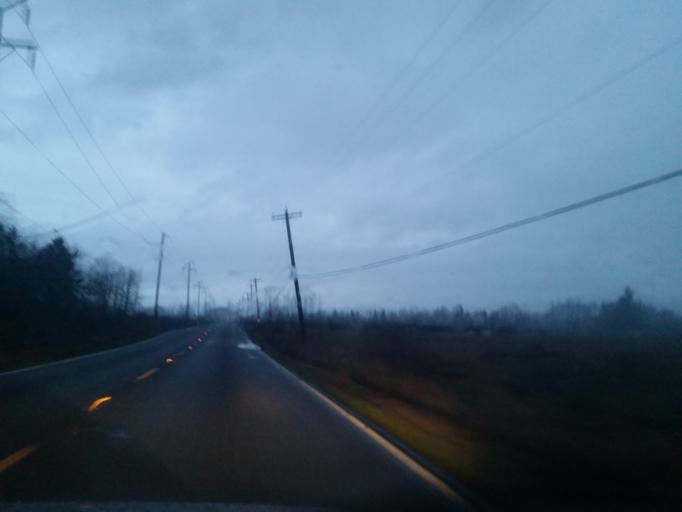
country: US
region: Washington
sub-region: Snohomish County
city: Everett
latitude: 47.9695
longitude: -122.1736
